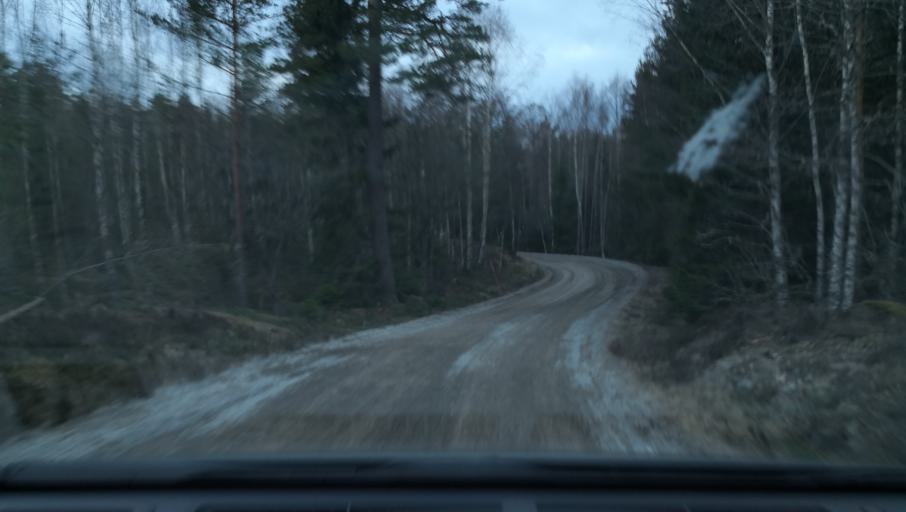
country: SE
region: Vaestmanland
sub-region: Kopings Kommun
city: Kolsva
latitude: 59.5642
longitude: 15.7953
